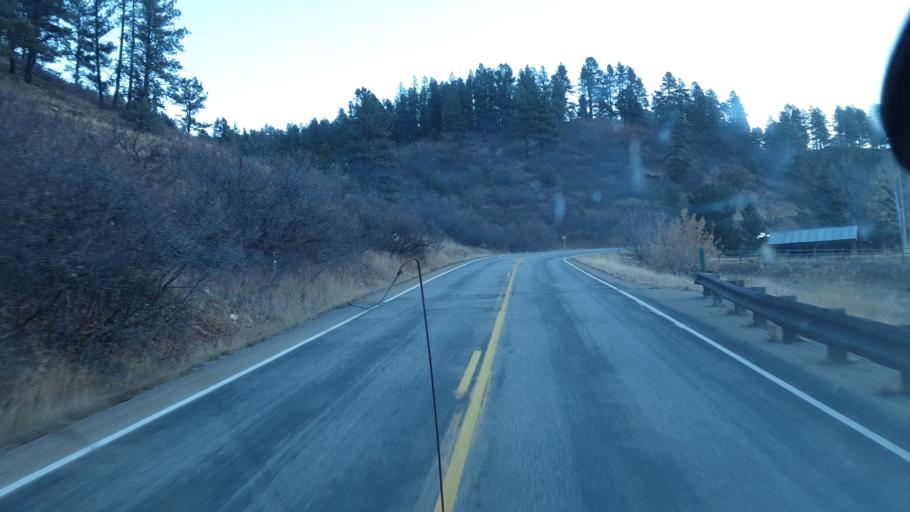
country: US
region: Colorado
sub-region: La Plata County
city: Durango
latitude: 37.3324
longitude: -107.7436
